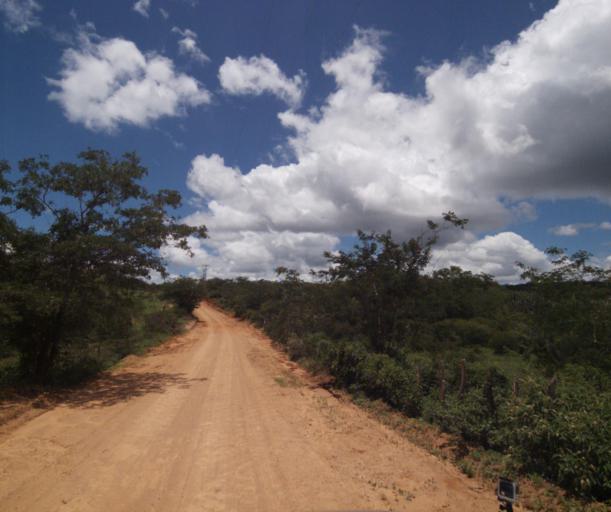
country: BR
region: Bahia
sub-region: Pocoes
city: Pocoes
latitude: -14.3795
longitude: -40.3937
